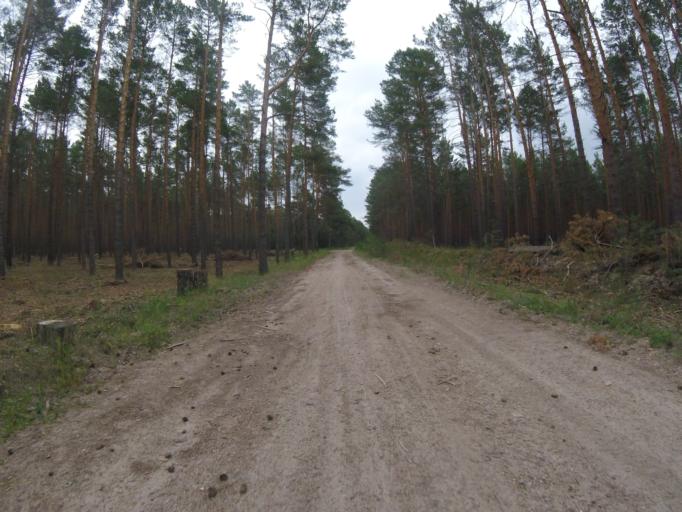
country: DE
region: Brandenburg
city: Gross Koris
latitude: 52.1936
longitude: 13.6834
